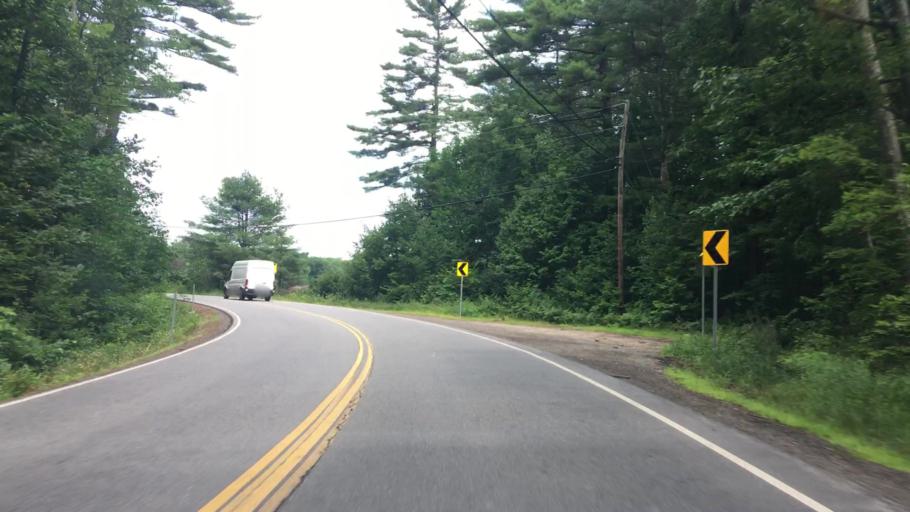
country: US
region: New Hampshire
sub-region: Belknap County
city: Laconia
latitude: 43.5771
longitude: -71.5049
